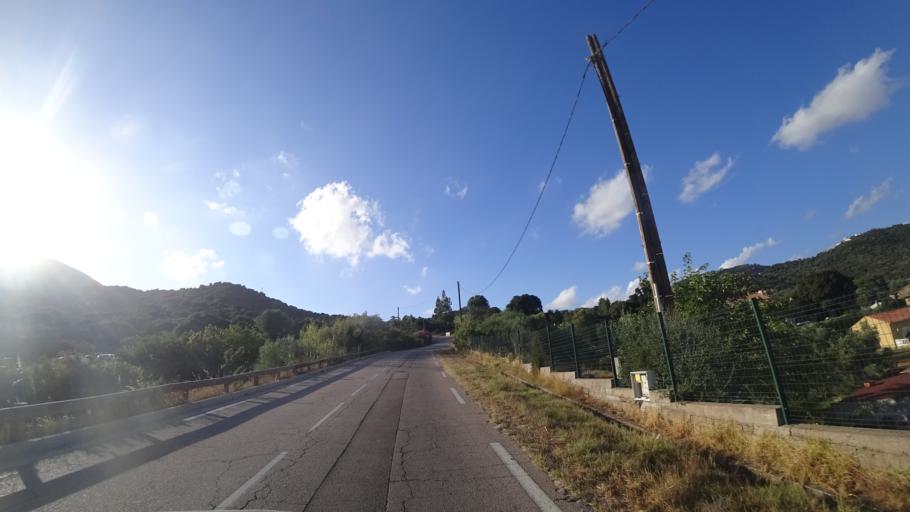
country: FR
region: Corsica
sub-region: Departement de la Corse-du-Sud
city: Alata
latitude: 41.9563
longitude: 8.7284
